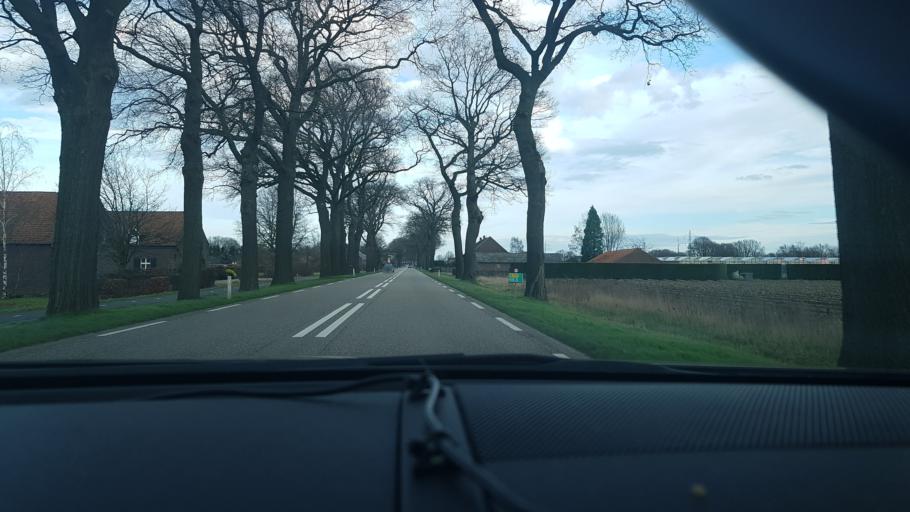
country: NL
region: Limburg
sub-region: Gemeente Beesel
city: Beesel
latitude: 51.2890
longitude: 6.0349
